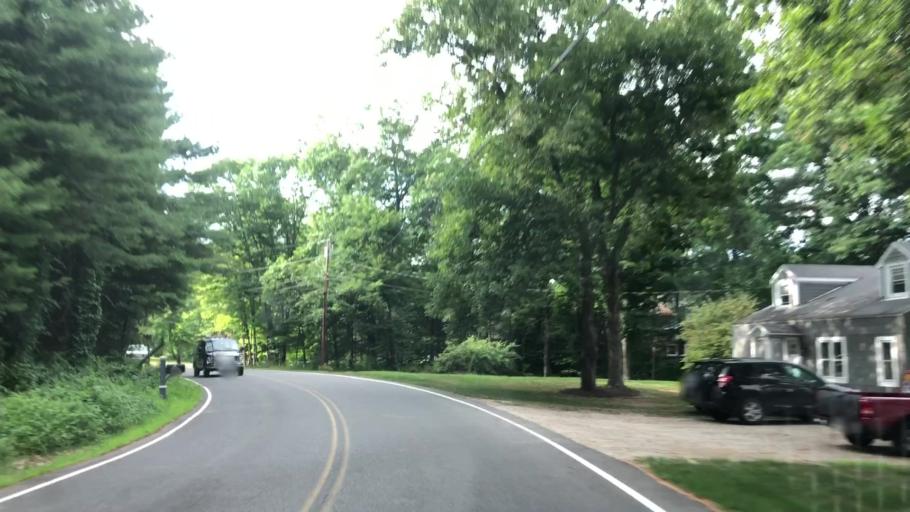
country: US
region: Massachusetts
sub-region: Hampshire County
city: Southampton
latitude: 42.2188
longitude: -72.7460
